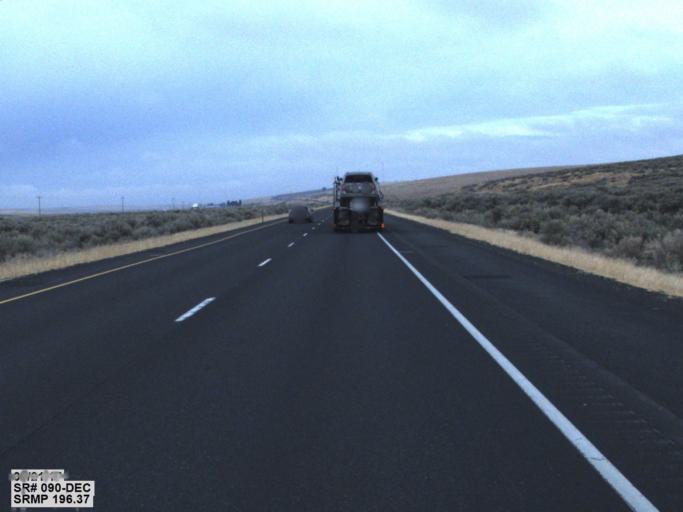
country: US
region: Washington
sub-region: Grant County
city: Warden
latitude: 47.0874
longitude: -118.8864
